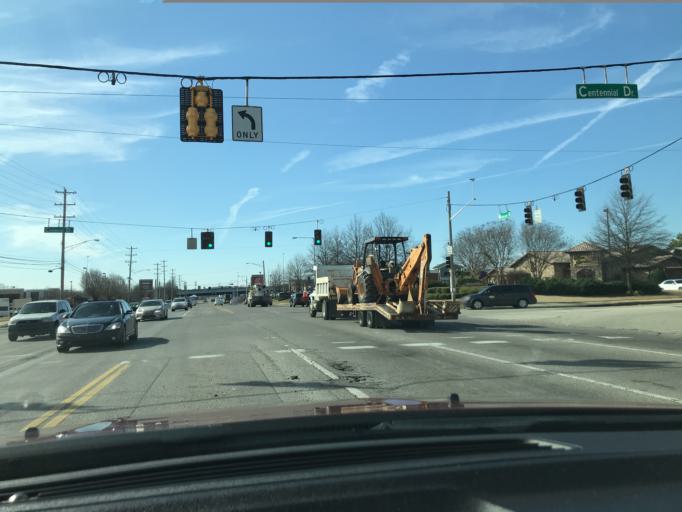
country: US
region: Tennessee
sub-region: Shelby County
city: Germantown
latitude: 35.0492
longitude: -89.8035
